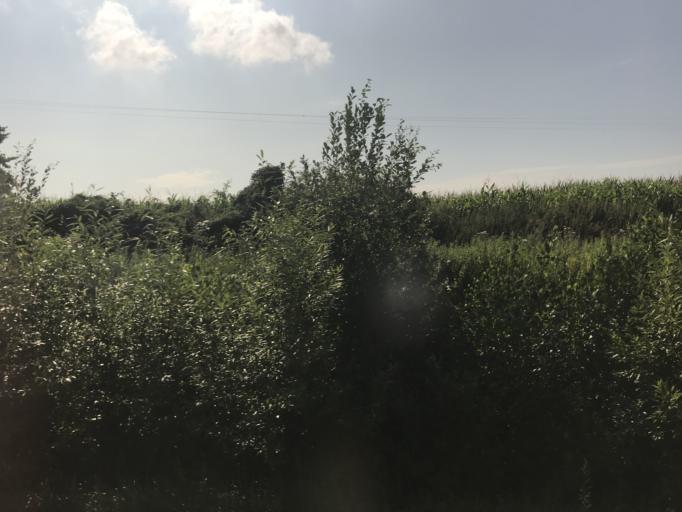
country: PL
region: Kujawsko-Pomorskie
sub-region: Powiat swiecki
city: Bukowiec
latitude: 53.3892
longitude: 18.3218
